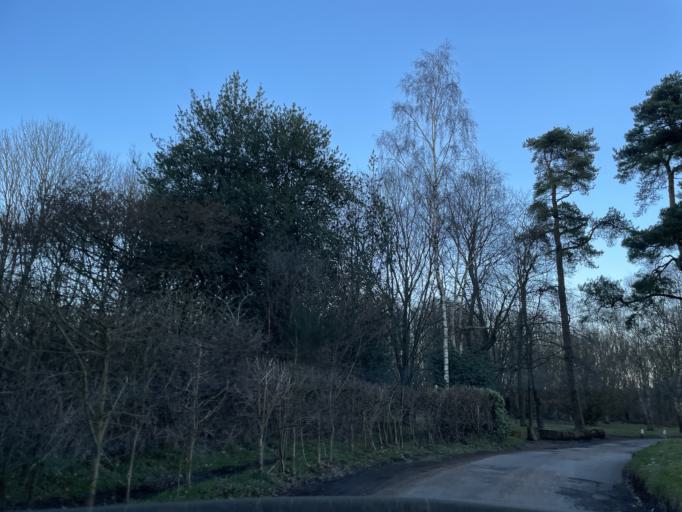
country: GB
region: England
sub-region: Kent
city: Westerham
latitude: 51.2552
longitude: 0.1197
